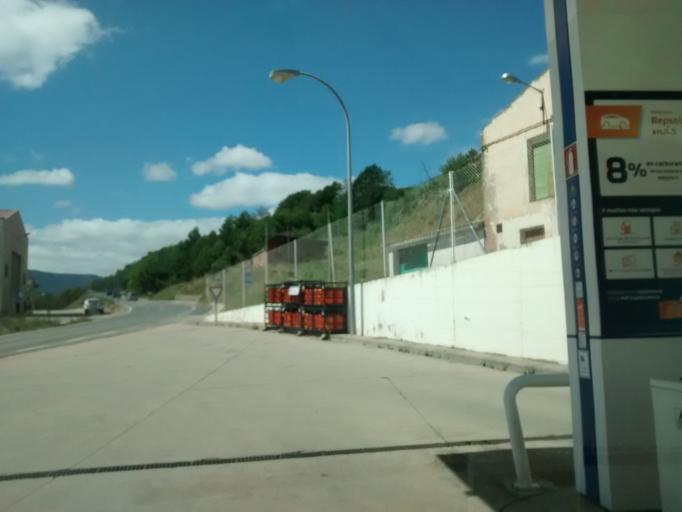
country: ES
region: La Rioja
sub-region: Provincia de La Rioja
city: Murillo de Rio Leza
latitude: 42.3994
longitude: -2.3340
